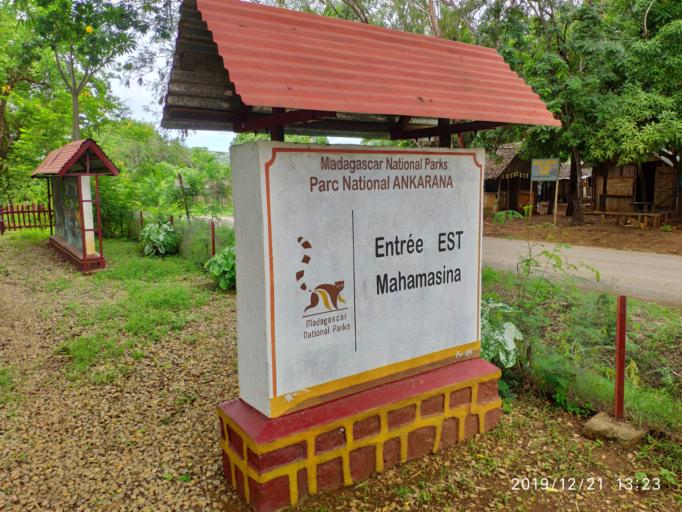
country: MG
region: Diana
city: Ambilobe
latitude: -12.9683
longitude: 49.1386
